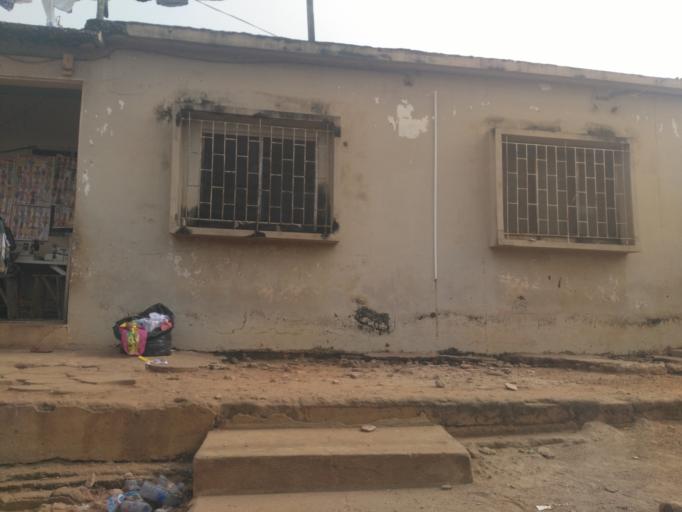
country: GH
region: Ashanti
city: Kumasi
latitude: 6.7030
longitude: -1.6323
